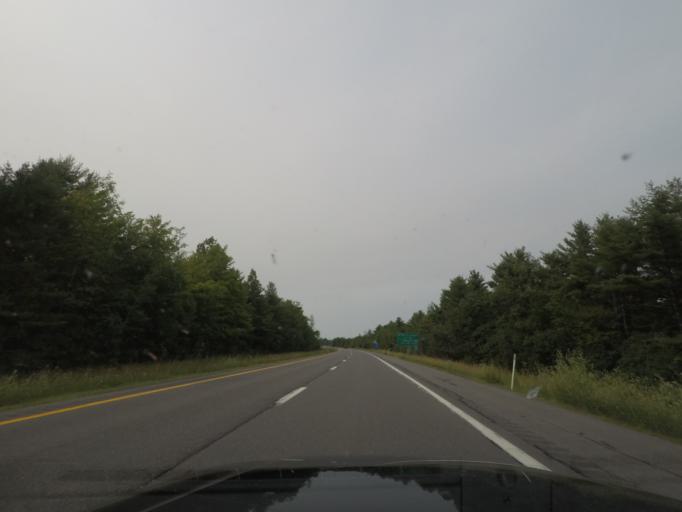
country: US
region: New York
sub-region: Clinton County
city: Champlain
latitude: 44.9658
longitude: -73.4498
